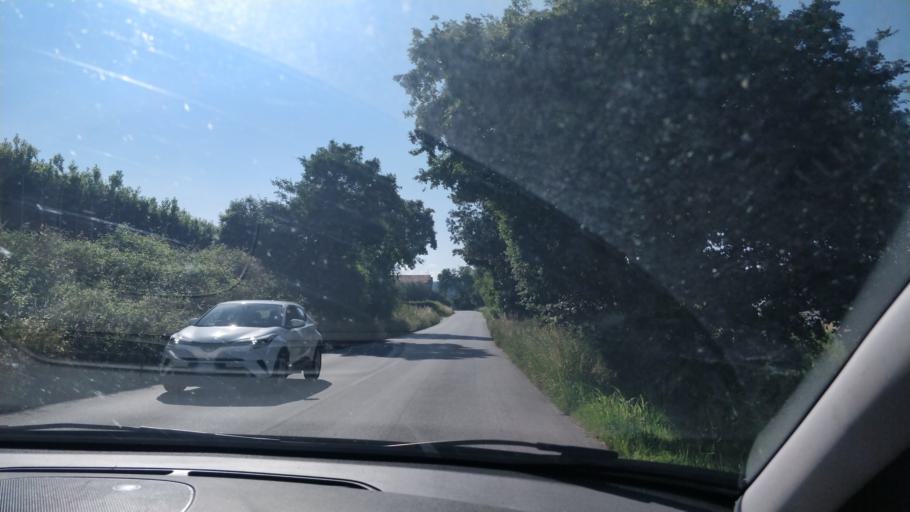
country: IT
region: The Marches
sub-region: Provincia di Ascoli Piceno
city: Cupra Marittima
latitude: 43.0349
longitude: 13.8452
